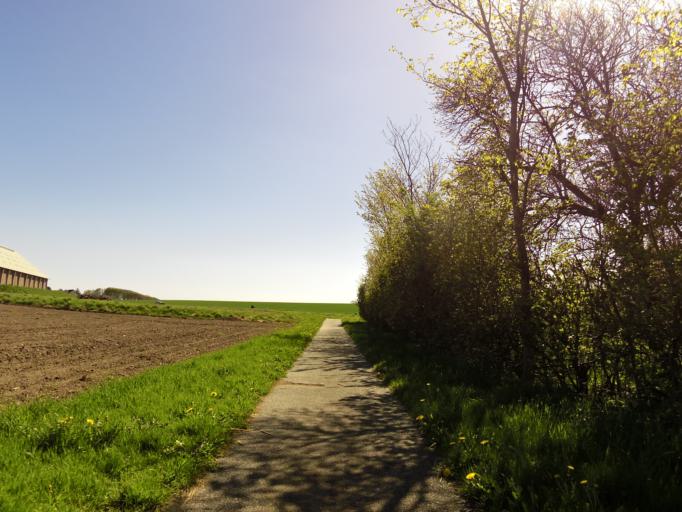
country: DK
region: Central Jutland
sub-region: Holstebro Kommune
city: Vinderup
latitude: 56.5991
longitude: 8.7737
